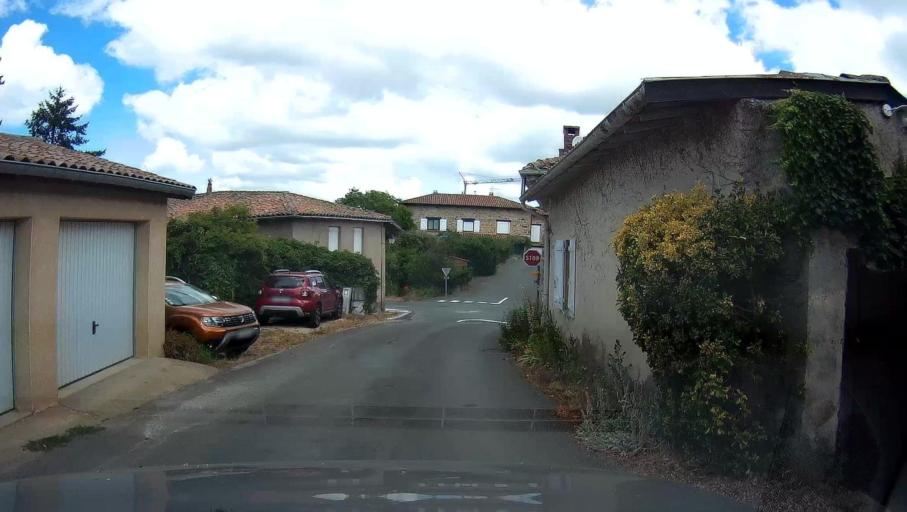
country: FR
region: Rhone-Alpes
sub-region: Departement du Rhone
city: Le Perreon
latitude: 46.0263
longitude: 4.5566
